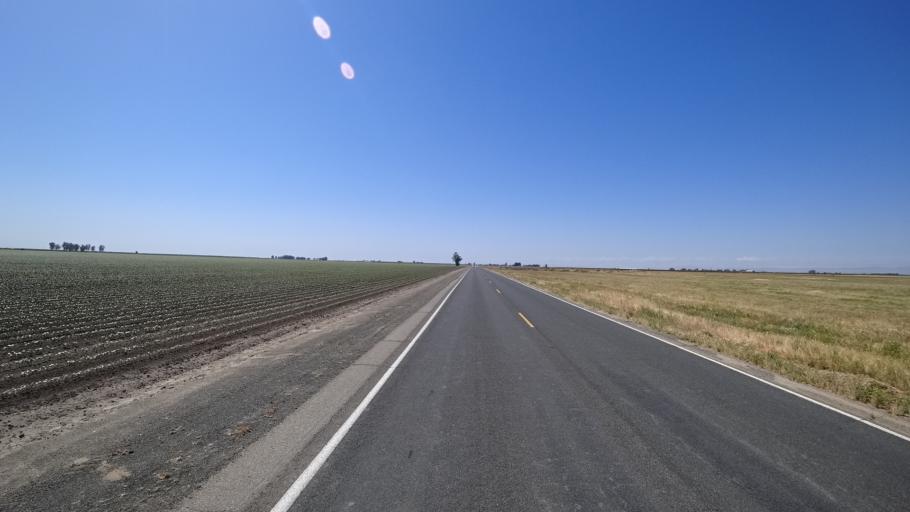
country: US
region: California
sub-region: Kings County
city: Stratford
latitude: 36.1945
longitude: -119.7802
